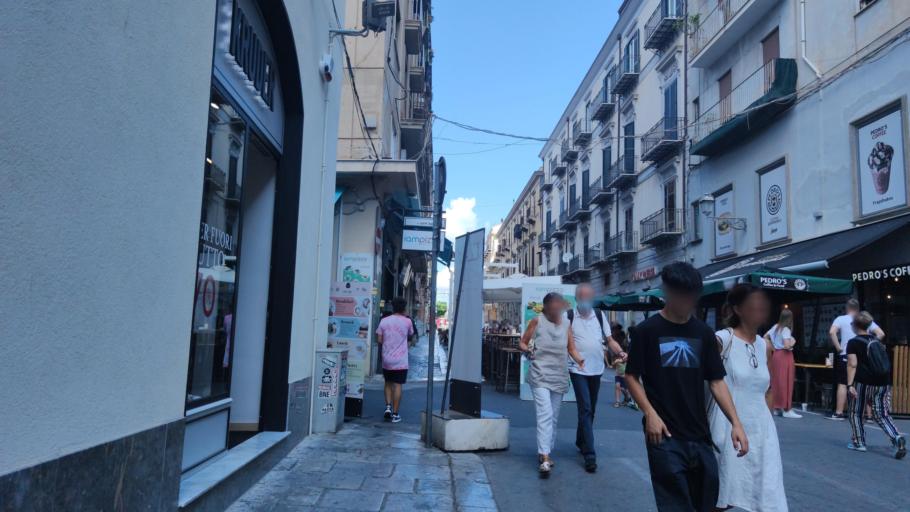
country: IT
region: Sicily
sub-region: Palermo
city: Palermo
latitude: 38.1184
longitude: 13.3597
